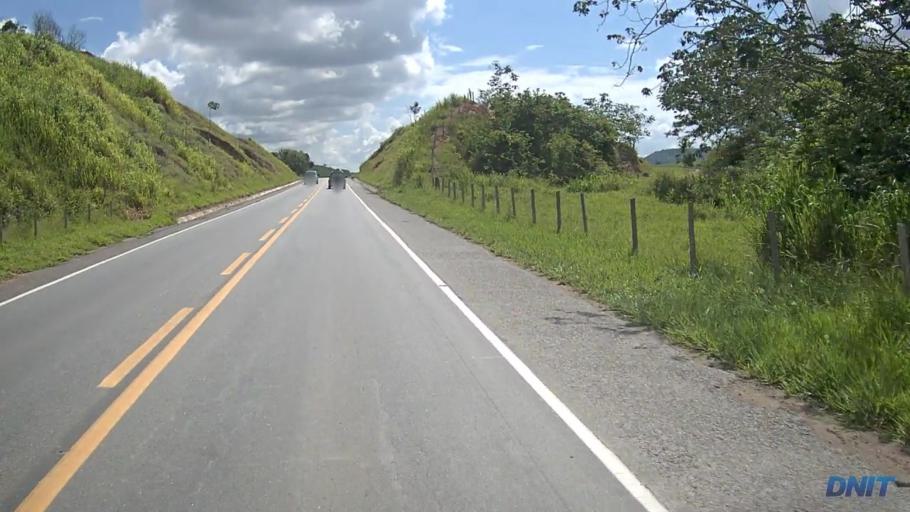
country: BR
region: Minas Gerais
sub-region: Governador Valadares
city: Governador Valadares
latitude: -18.9975
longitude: -42.1220
